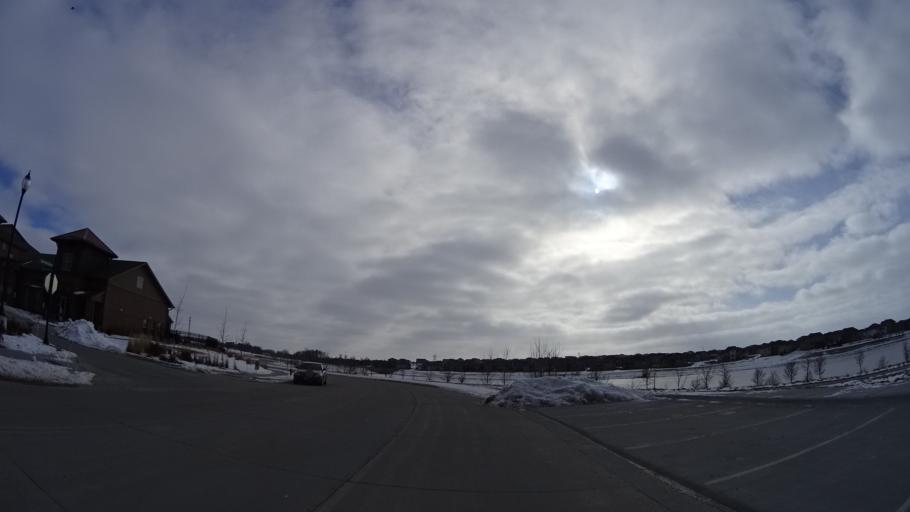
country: US
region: Nebraska
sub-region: Sarpy County
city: Papillion
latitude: 41.1315
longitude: -96.0265
